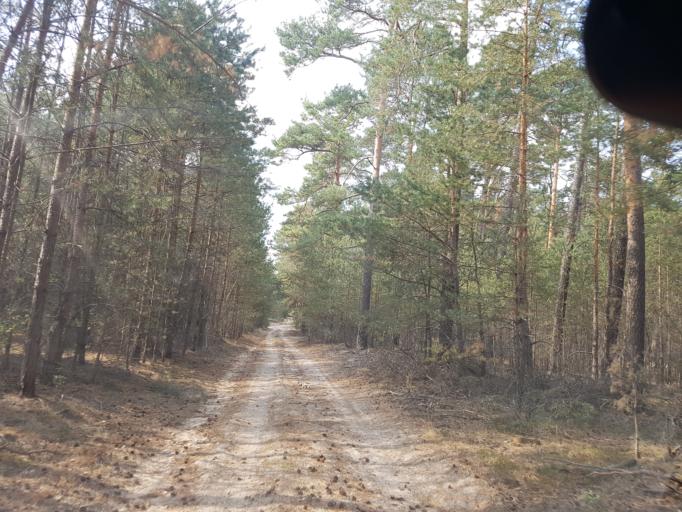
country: DE
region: Brandenburg
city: Treuenbrietzen
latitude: 52.0289
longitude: 12.8874
